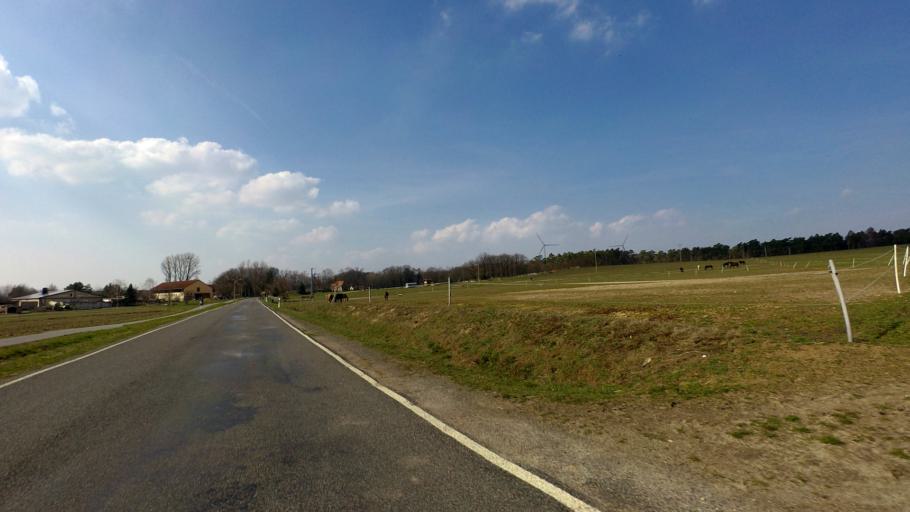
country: DE
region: Brandenburg
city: Ihlow
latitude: 51.9504
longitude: 13.3709
